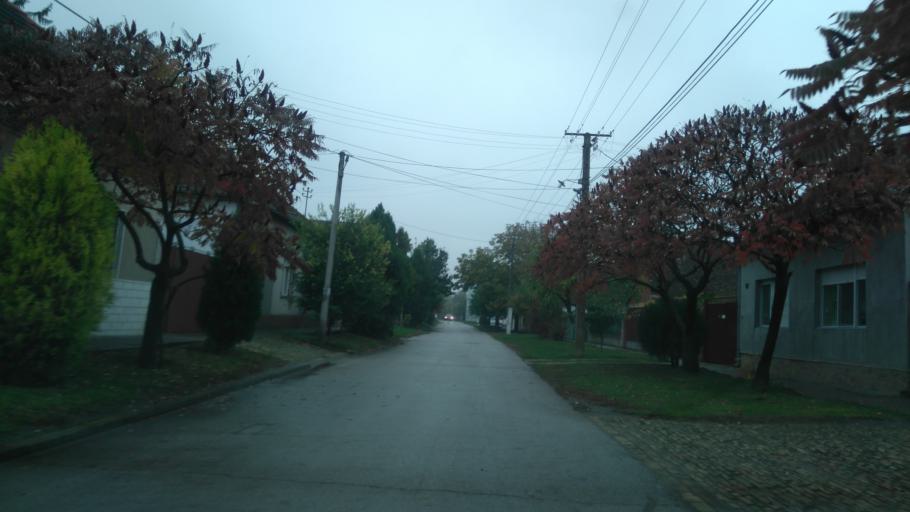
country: RS
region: Autonomna Pokrajina Vojvodina
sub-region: Juznobacki Okrug
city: Becej
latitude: 45.6235
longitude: 20.0492
